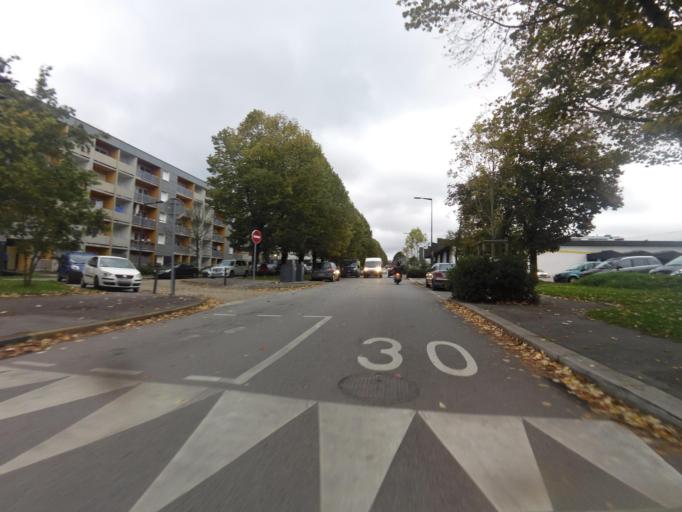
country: FR
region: Brittany
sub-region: Departement du Morbihan
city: Vannes
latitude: 47.6729
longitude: -2.7676
